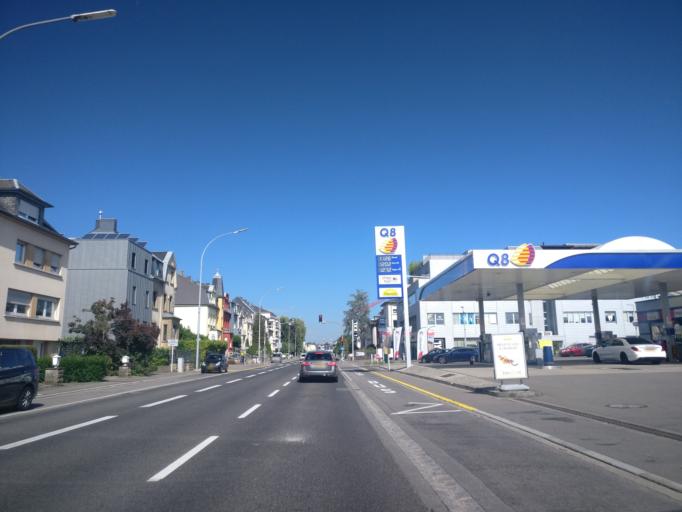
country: LU
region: Luxembourg
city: Bereldange
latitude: 49.6529
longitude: 6.1275
